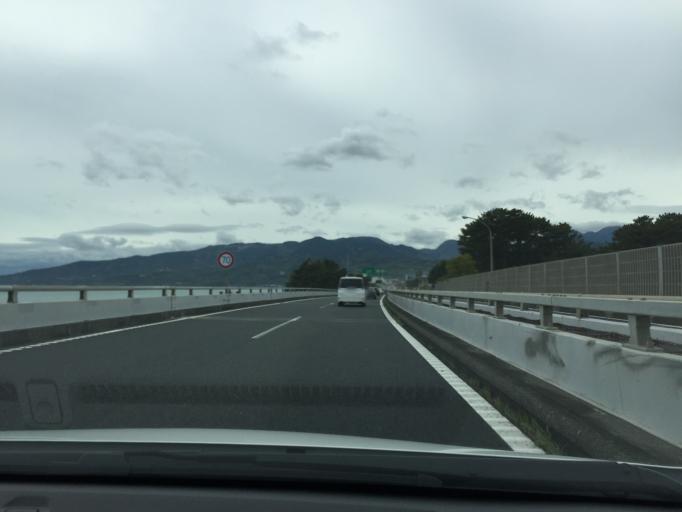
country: JP
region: Kanagawa
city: Odawara
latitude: 35.2599
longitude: 139.1819
